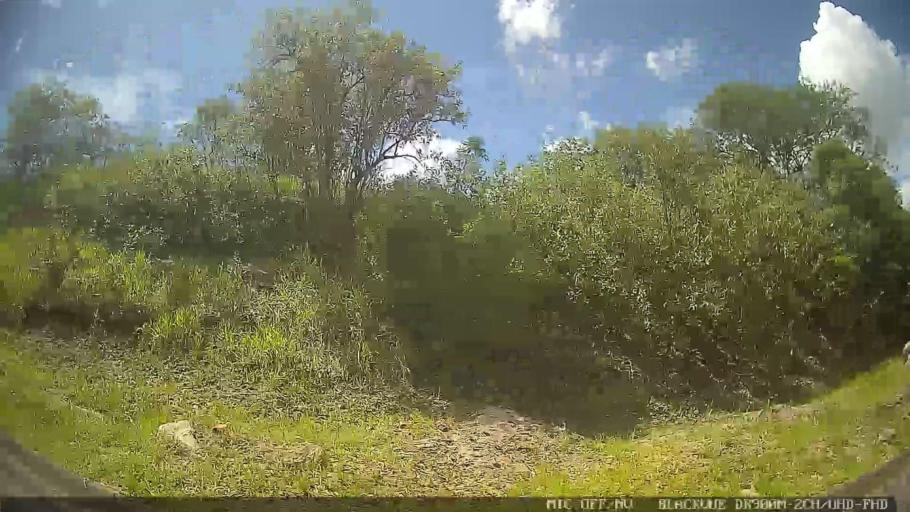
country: BR
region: Sao Paulo
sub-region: Conchas
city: Conchas
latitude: -23.0260
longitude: -48.0004
